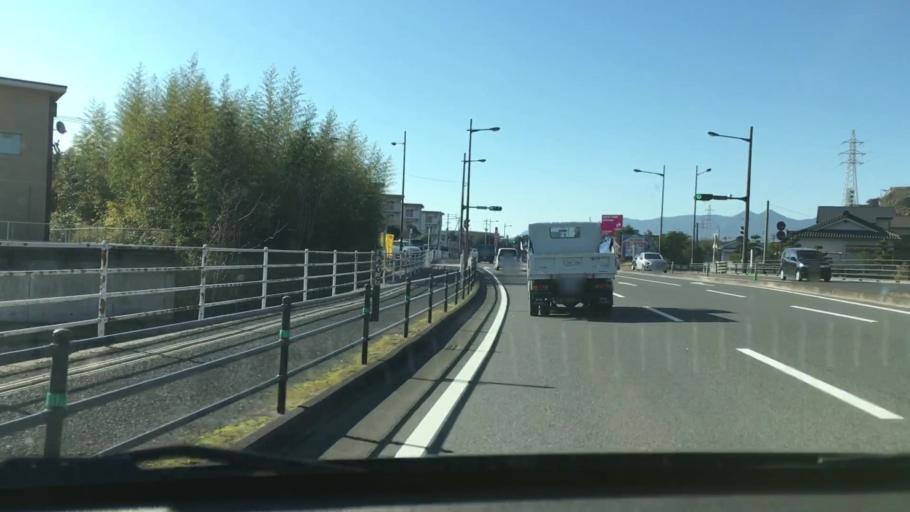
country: JP
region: Kagoshima
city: Kajiki
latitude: 31.7411
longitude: 130.6524
